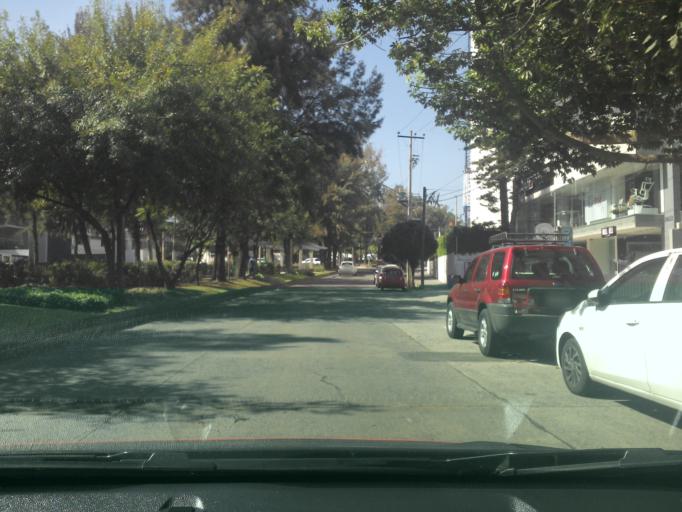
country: MX
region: Jalisco
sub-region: Zapopan
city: Zapopan
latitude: 20.6974
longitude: -103.3805
